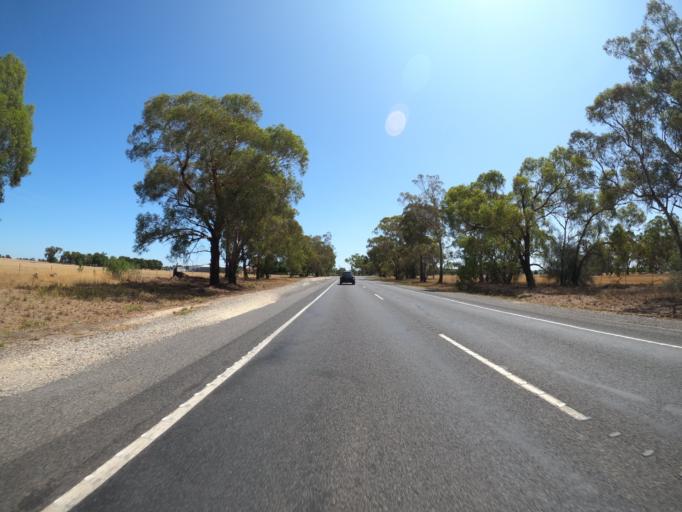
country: AU
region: New South Wales
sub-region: Corowa Shire
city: Corowa
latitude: -36.0584
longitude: 146.4342
